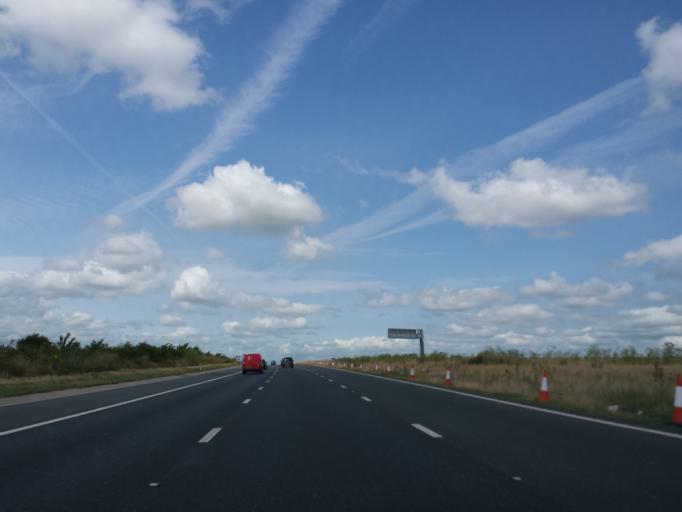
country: GB
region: England
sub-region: North Yorkshire
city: Ripon
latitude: 54.1709
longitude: -1.4519
